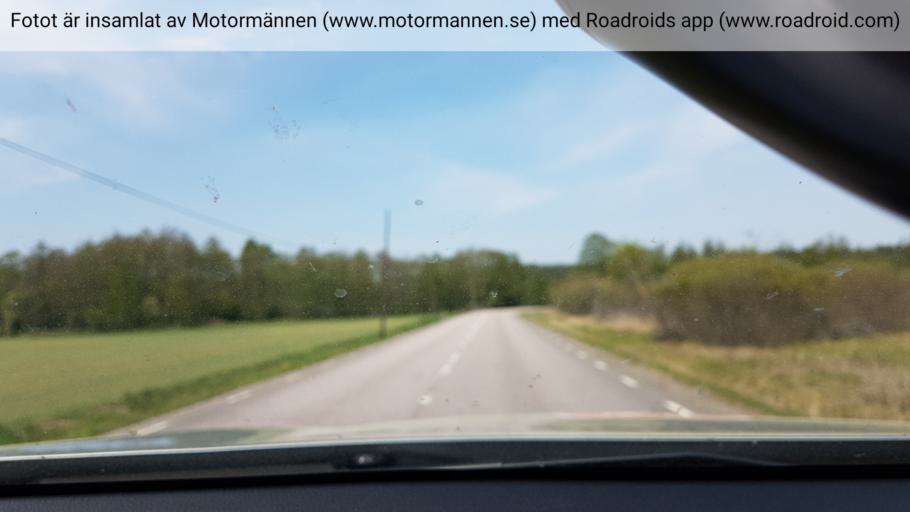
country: SE
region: Stockholm
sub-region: Botkyrka Kommun
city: Varsta
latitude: 59.1181
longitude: 17.8547
